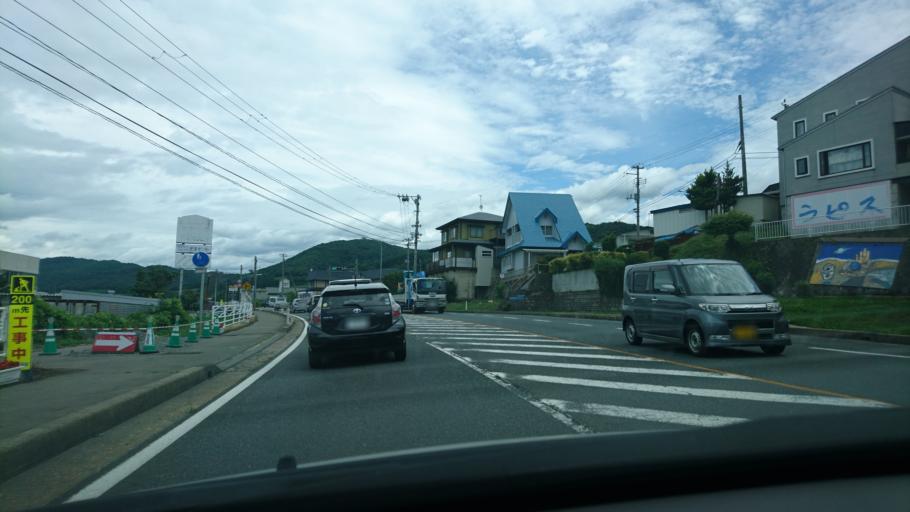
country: JP
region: Iwate
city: Morioka-shi
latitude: 39.6368
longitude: 141.1858
